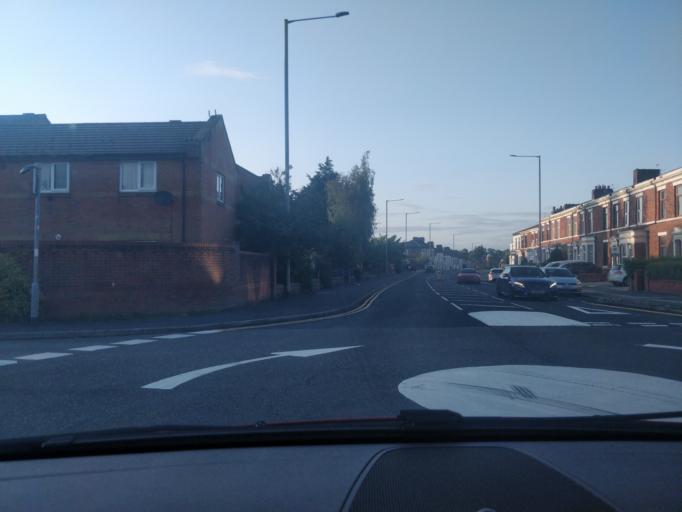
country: GB
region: England
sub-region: Lancashire
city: Preston
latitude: 53.7657
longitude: -2.6916
